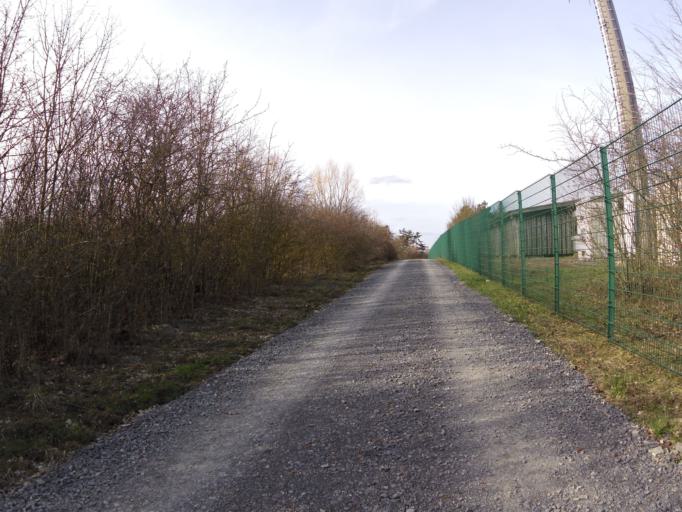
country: DE
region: Bavaria
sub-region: Regierungsbezirk Unterfranken
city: Hettstadt
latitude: 49.8272
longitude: 9.8204
